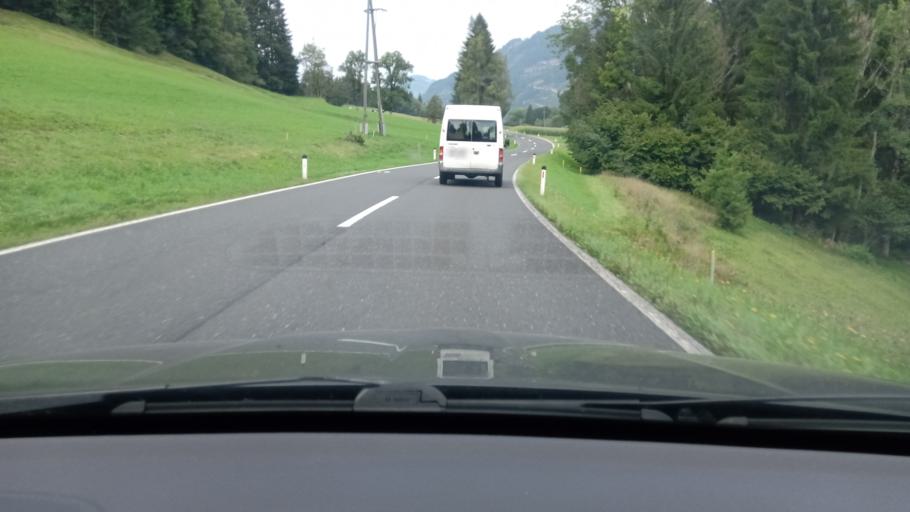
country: AT
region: Carinthia
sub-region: Politischer Bezirk Hermagor
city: Hermagor
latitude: 46.6529
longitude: 13.3249
